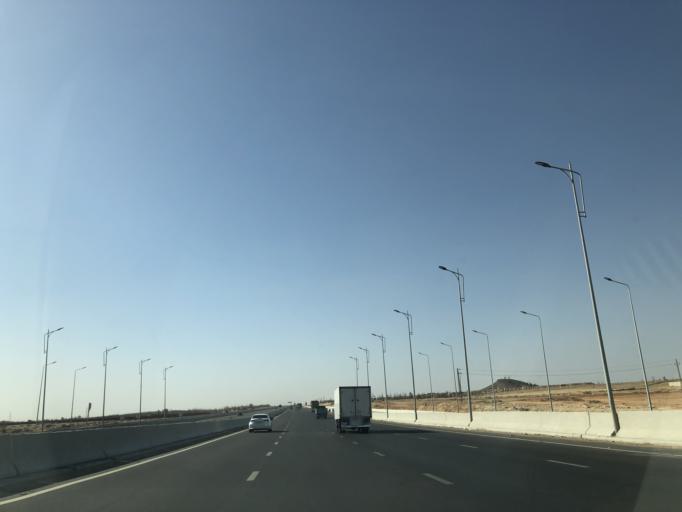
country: EG
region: Al Jizah
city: Madinat Sittah Uktubar
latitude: 29.9764
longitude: 30.8680
